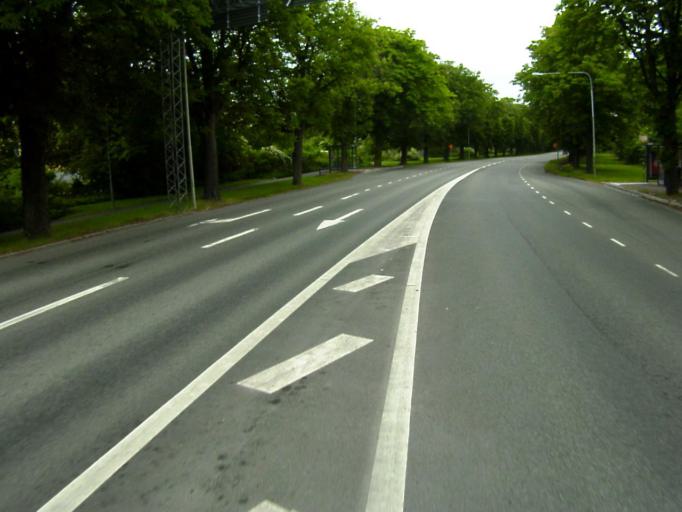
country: SE
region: Skane
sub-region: Kristianstads Kommun
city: Kristianstad
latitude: 56.0447
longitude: 14.1558
